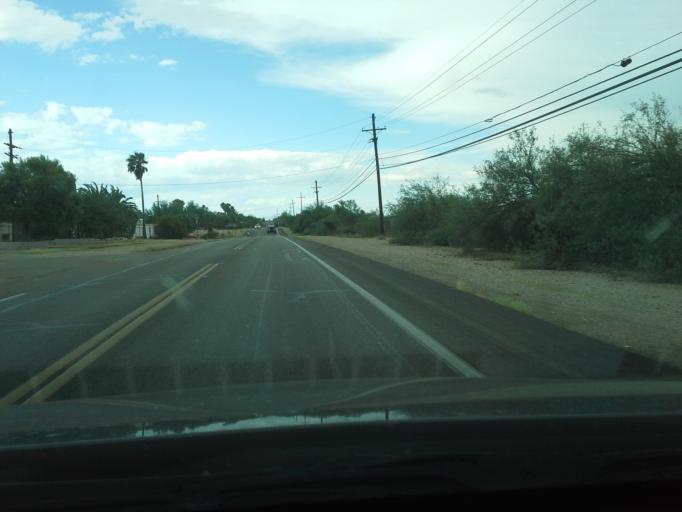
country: US
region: Arizona
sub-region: Pima County
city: South Tucson
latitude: 32.2152
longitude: -111.0203
